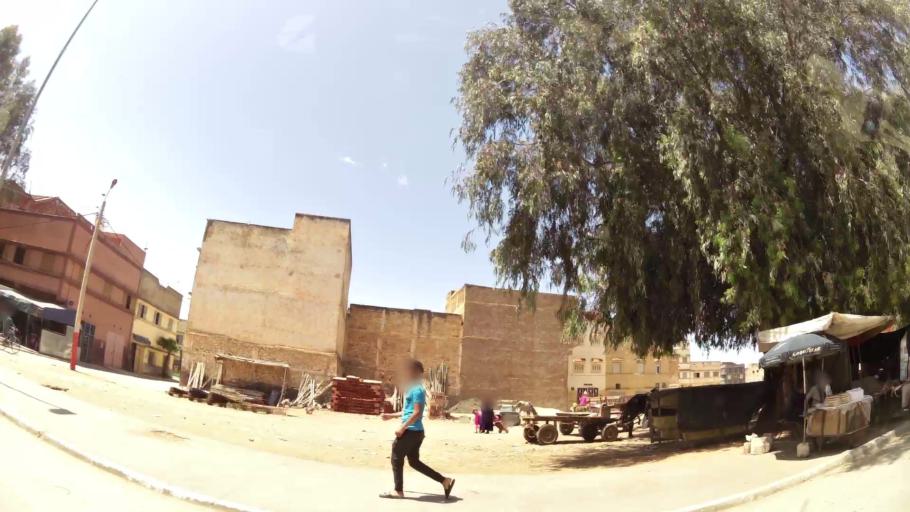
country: MA
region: Rabat-Sale-Zemmour-Zaer
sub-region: Khemisset
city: Khemisset
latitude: 33.8354
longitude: -6.0667
